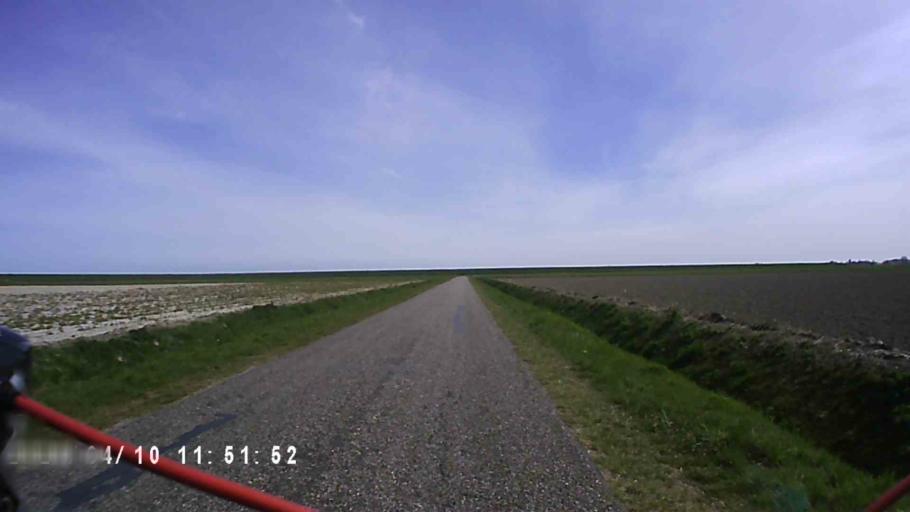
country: NL
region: Groningen
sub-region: Gemeente De Marne
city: Ulrum
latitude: 53.3933
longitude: 6.3266
